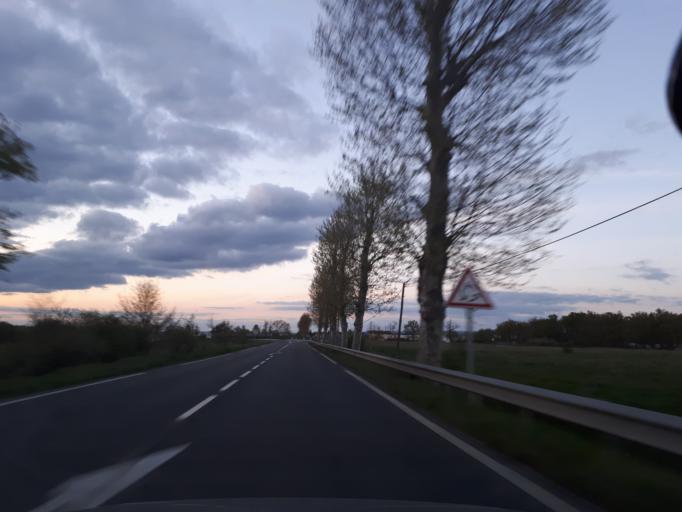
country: FR
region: Rhone-Alpes
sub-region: Departement de la Loire
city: Feurs
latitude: 45.7138
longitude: 4.2266
